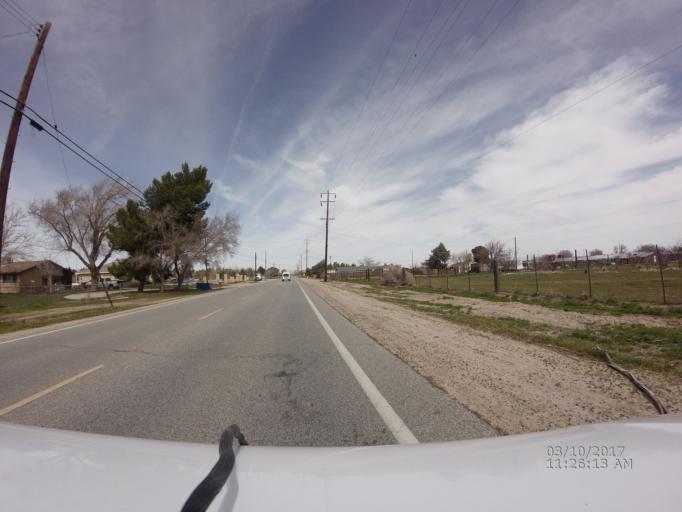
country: US
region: California
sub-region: Los Angeles County
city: Quartz Hill
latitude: 34.7497
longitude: -118.2899
